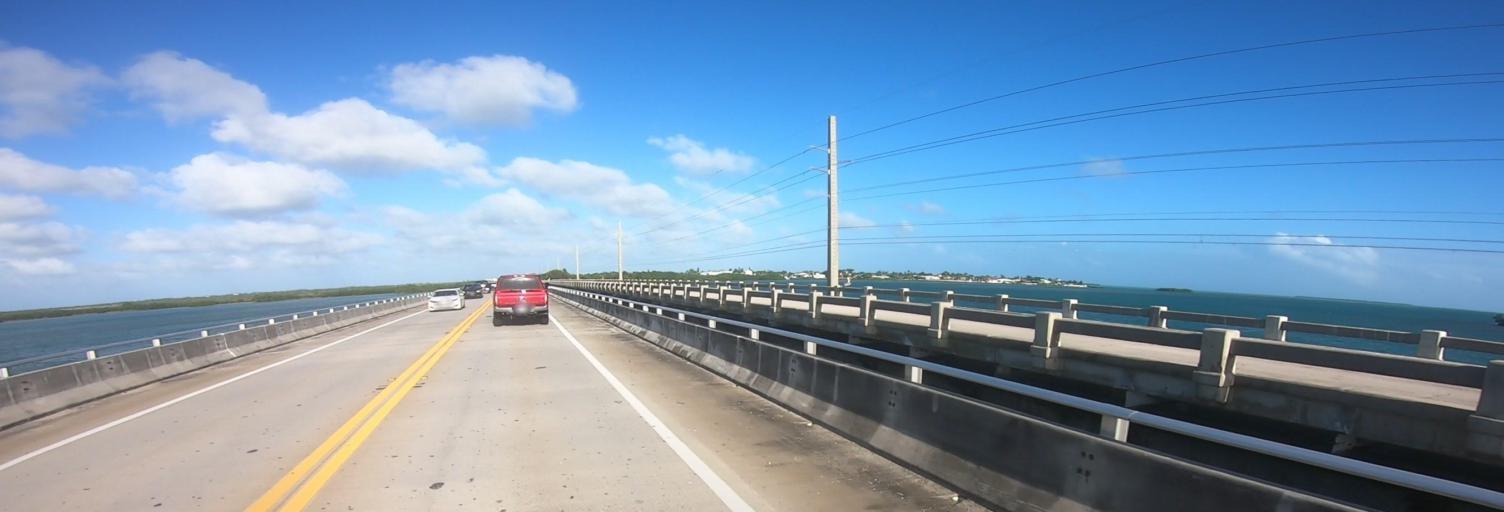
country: US
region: Florida
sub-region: Monroe County
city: Cudjoe Key
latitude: 24.6618
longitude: -81.5165
